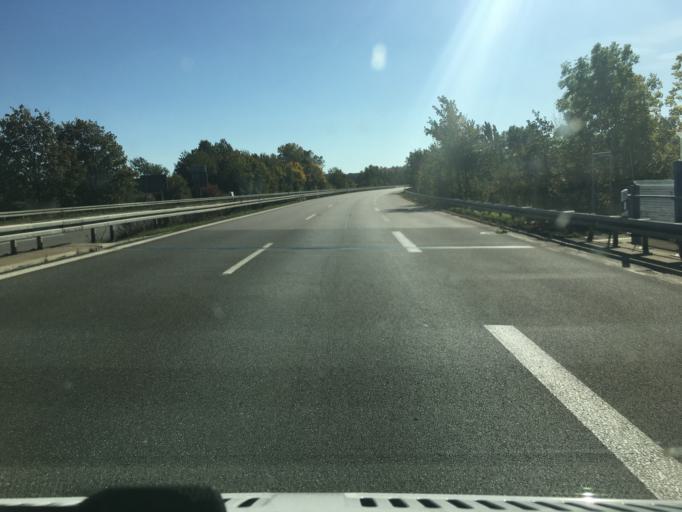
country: DE
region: Saxony
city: Dennheritz
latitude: 50.7823
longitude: 12.4920
